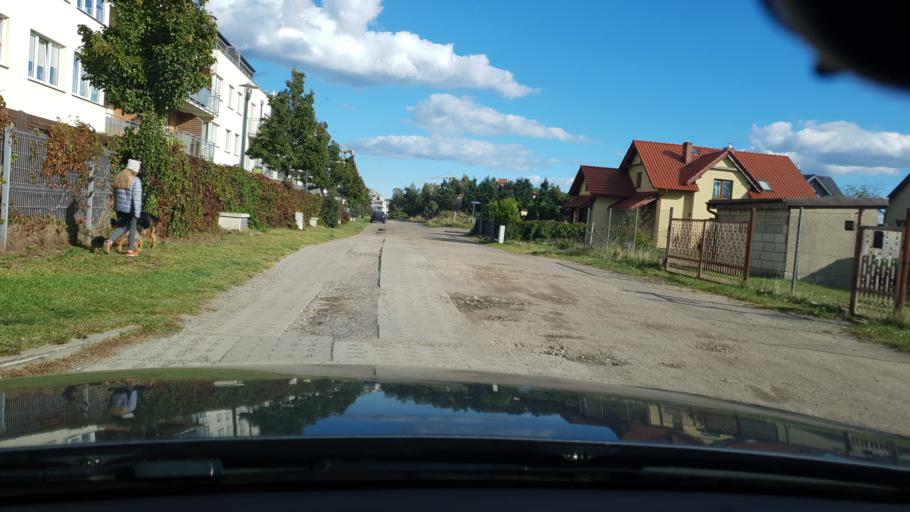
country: PL
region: Pomeranian Voivodeship
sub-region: Powiat kartuski
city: Chwaszczyno
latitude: 54.4927
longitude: 18.4383
